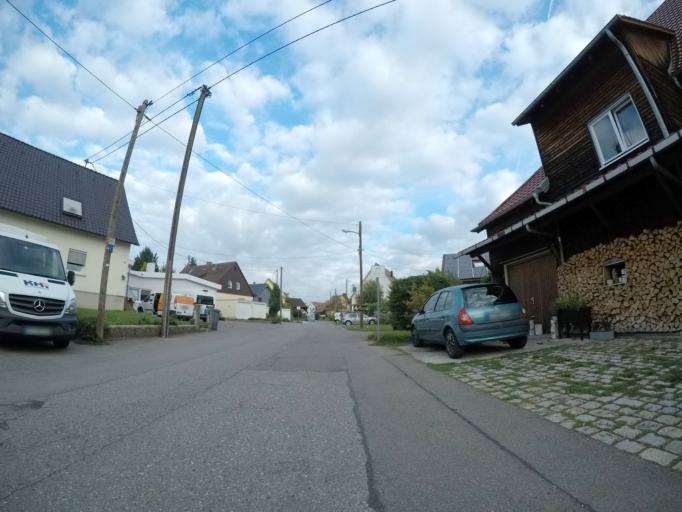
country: DE
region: Baden-Wuerttemberg
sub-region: Tuebingen Region
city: Sickenhausen
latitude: 48.5211
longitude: 9.1793
